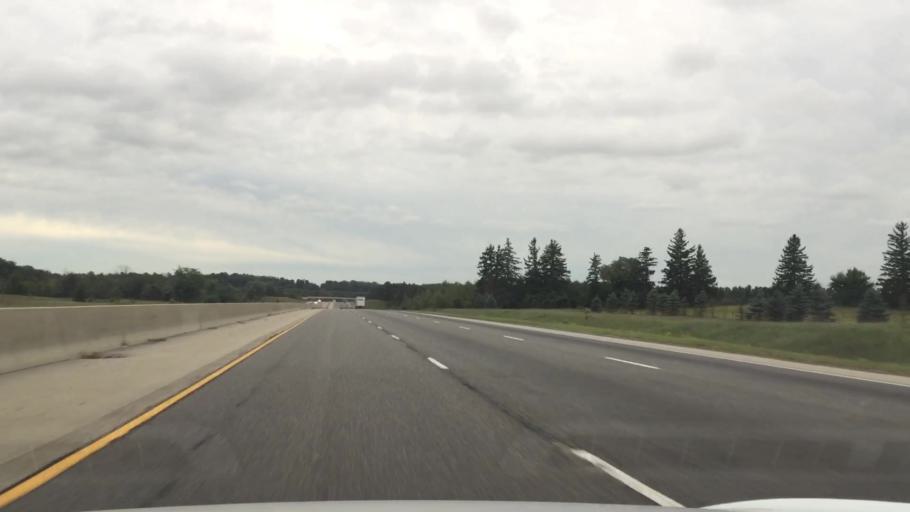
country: CA
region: Ontario
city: Kitchener
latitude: 43.3094
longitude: -80.4775
